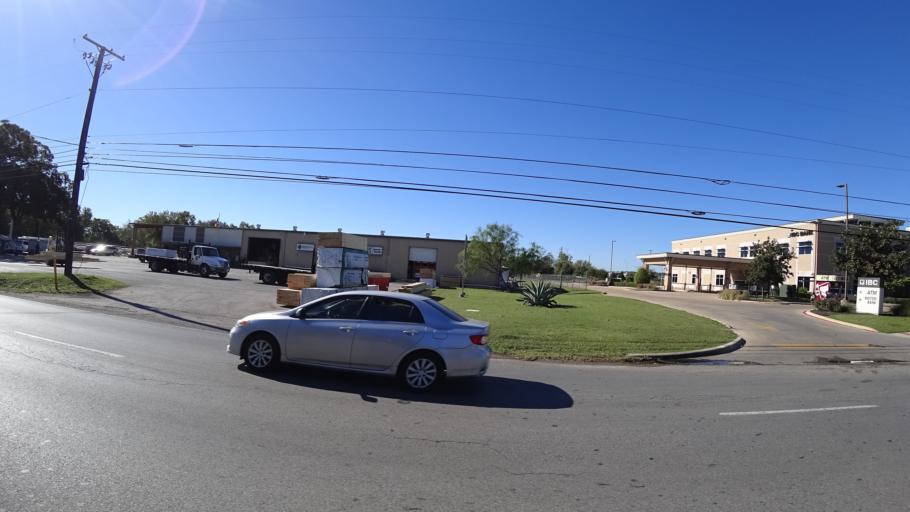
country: US
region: Texas
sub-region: Travis County
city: Austin
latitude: 30.2526
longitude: -97.7116
